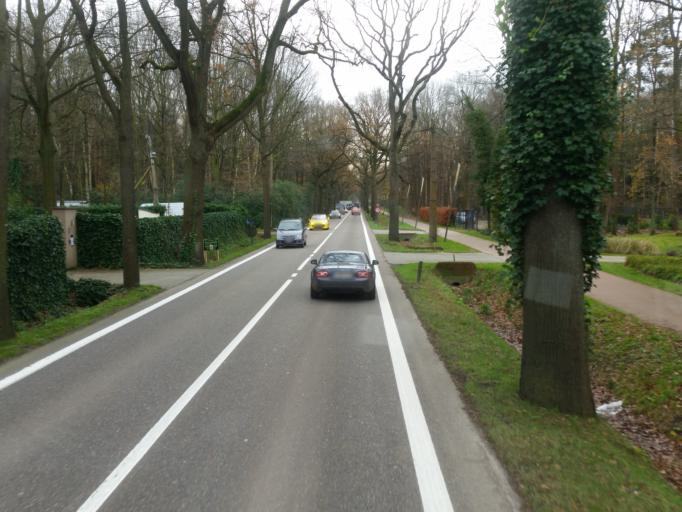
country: BE
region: Flanders
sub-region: Provincie Antwerpen
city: Kalmthout
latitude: 51.3524
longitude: 4.5088
